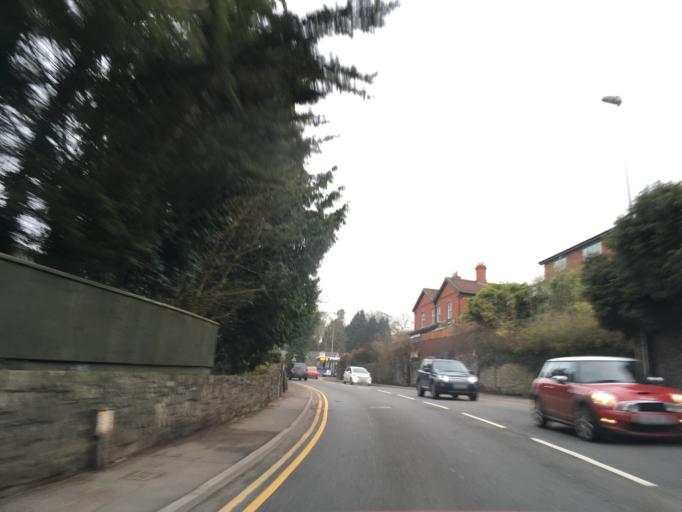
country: GB
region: Wales
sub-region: Monmouthshire
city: Chepstow
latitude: 51.6390
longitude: -2.6783
